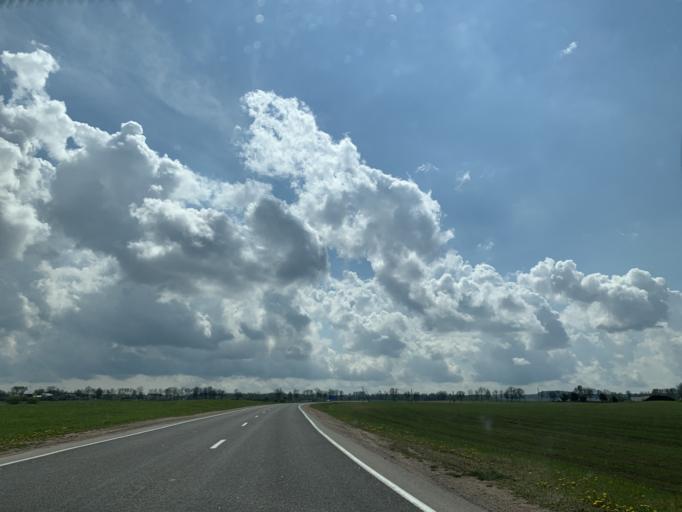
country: BY
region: Minsk
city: Nyasvizh
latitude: 53.2344
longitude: 26.7194
